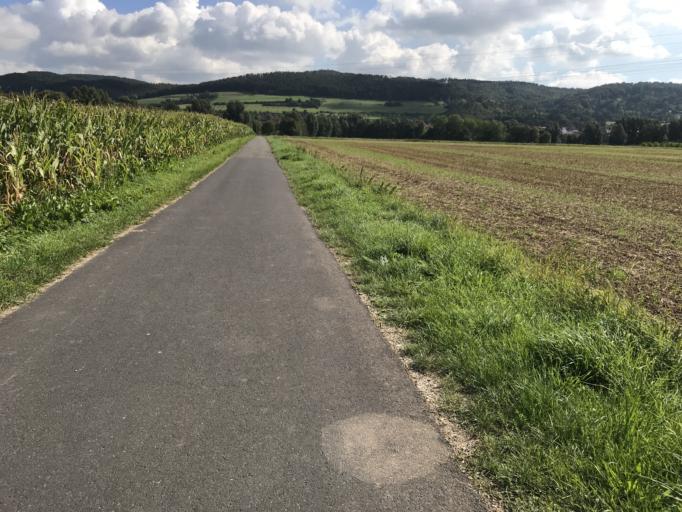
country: DE
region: Hesse
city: Witzenhausen
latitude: 51.3402
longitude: 9.8744
